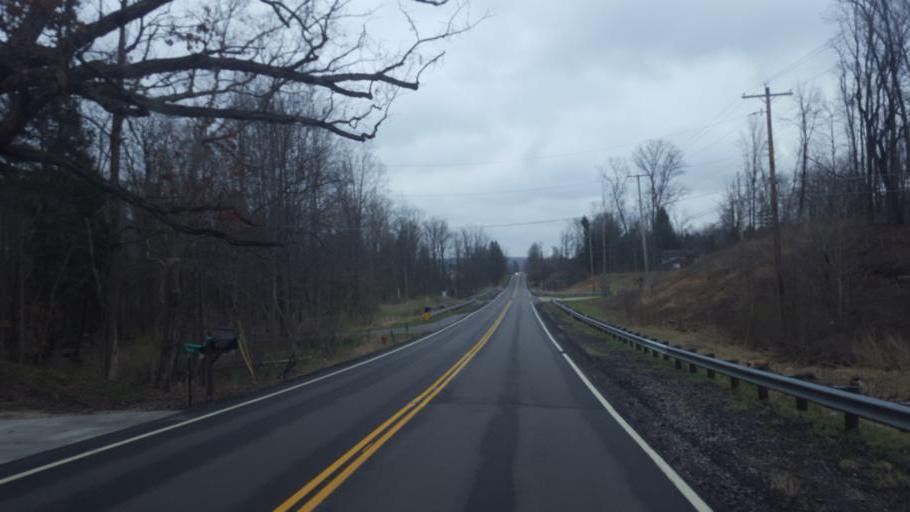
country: US
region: Ohio
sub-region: Medina County
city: Medina
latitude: 41.1066
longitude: -81.8300
